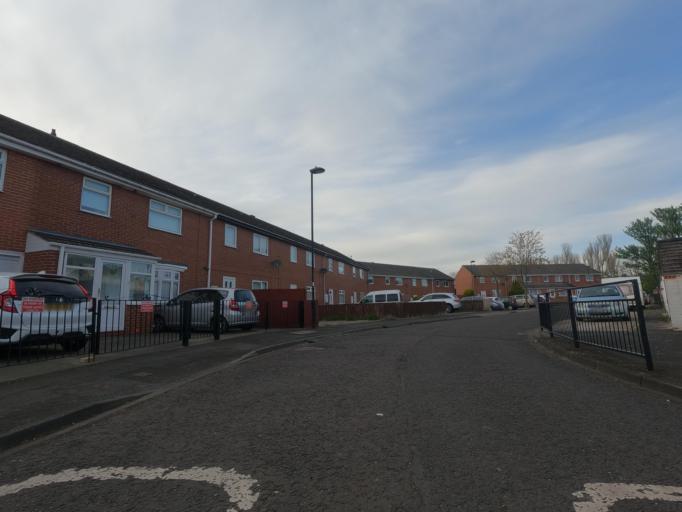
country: GB
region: England
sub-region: Newcastle upon Tyne
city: Hazlerigg
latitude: 55.0589
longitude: -1.6291
